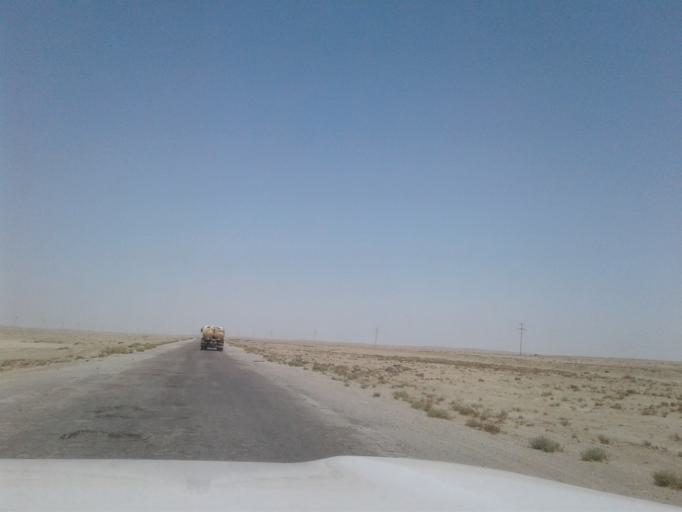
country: TM
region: Balkan
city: Gumdag
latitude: 38.3477
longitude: 54.3673
